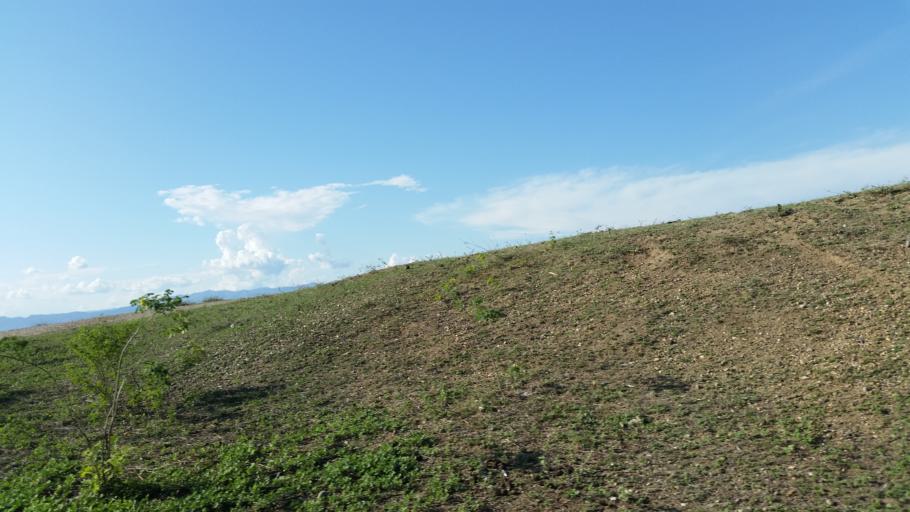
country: CO
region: Huila
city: Villavieja
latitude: 3.2340
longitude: -75.1194
